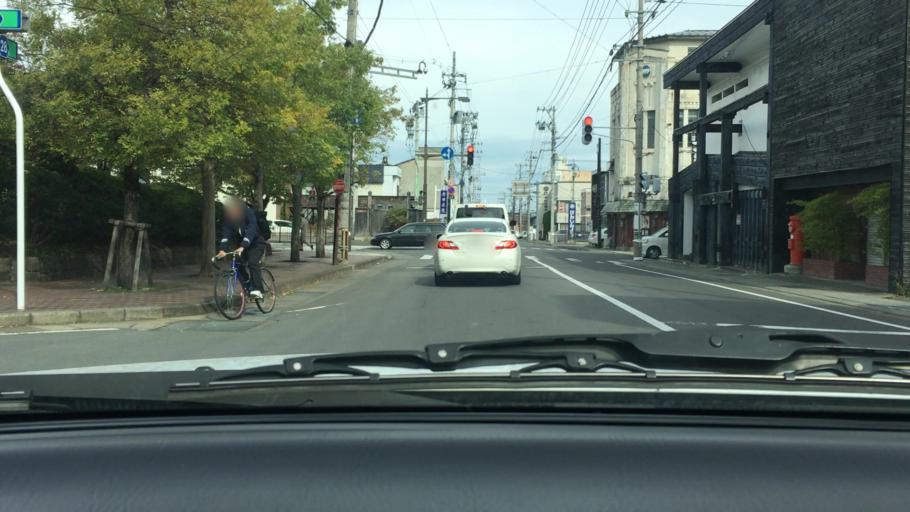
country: JP
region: Aomori
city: Hirosaki
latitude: 40.6030
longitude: 140.4695
